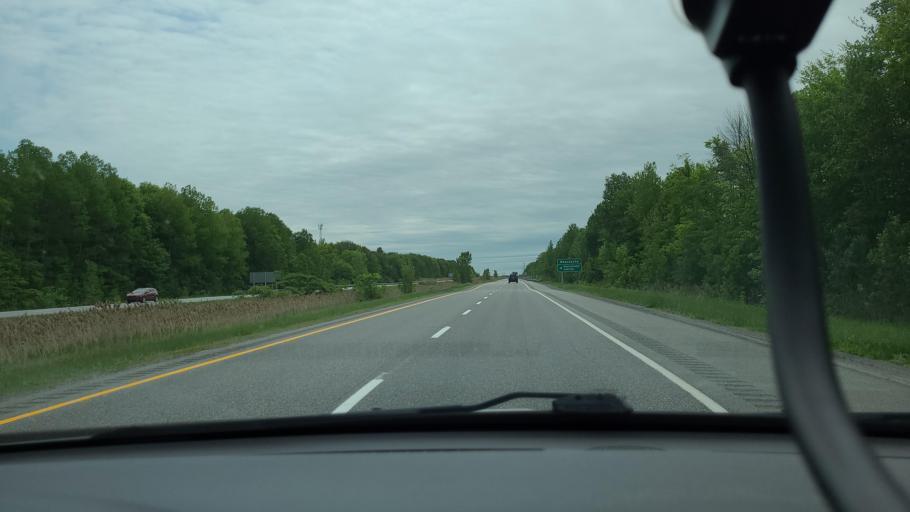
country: CA
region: Quebec
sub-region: Lanaudiere
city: Mascouche
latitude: 45.8095
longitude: -73.5927
